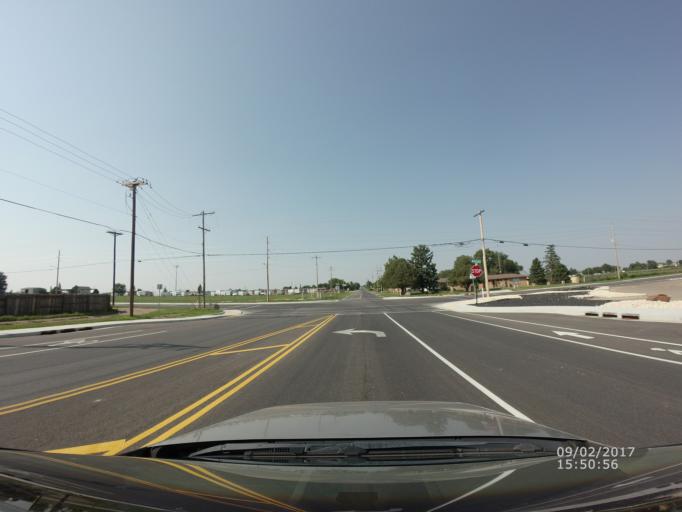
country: US
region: New Mexico
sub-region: Curry County
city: Clovis
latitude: 34.4479
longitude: -103.1785
